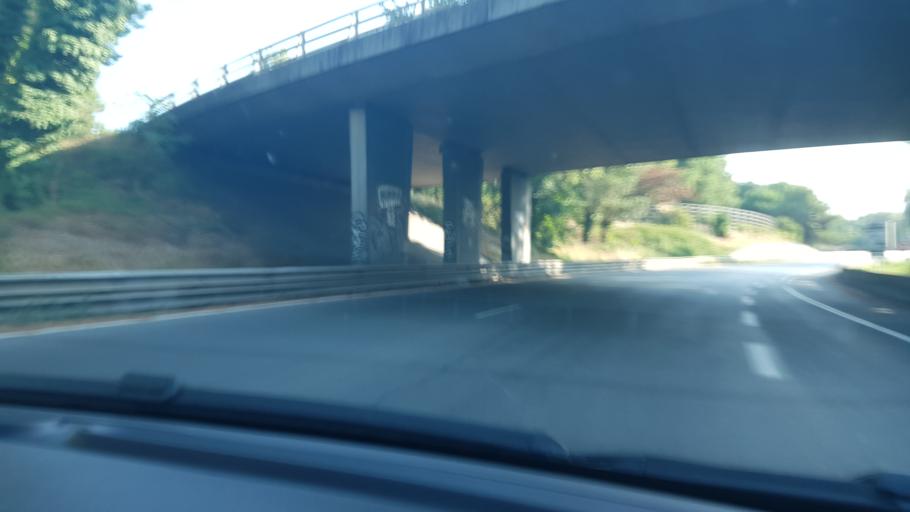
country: FR
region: Aquitaine
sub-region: Departement de la Gironde
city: Le Bouscat
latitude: 44.8831
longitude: -0.5619
